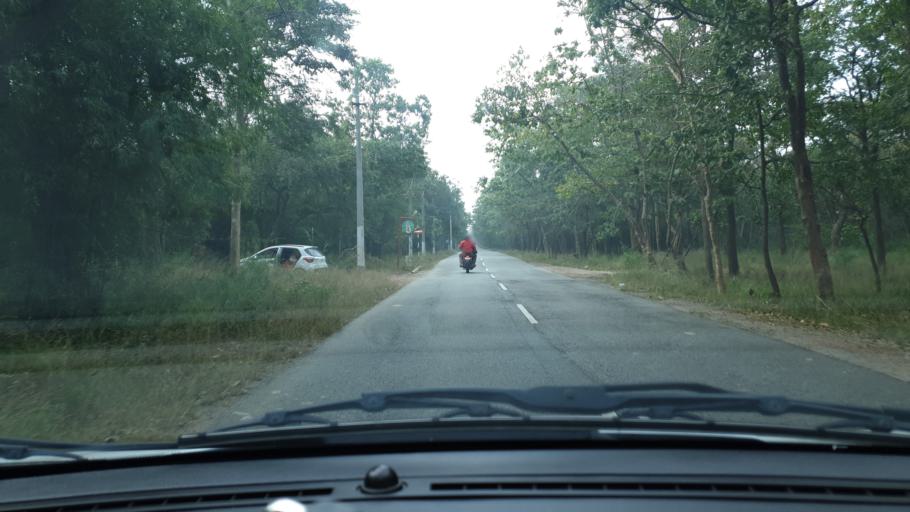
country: IN
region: Andhra Pradesh
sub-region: Kurnool
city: Srisailam
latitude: 16.2991
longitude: 78.7313
